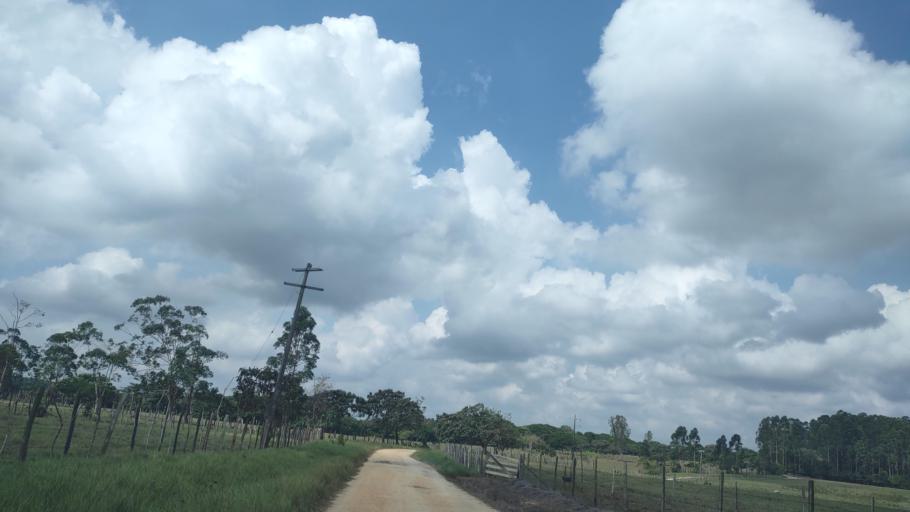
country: MX
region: Veracruz
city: Las Choapas
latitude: 17.9462
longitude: -94.0963
